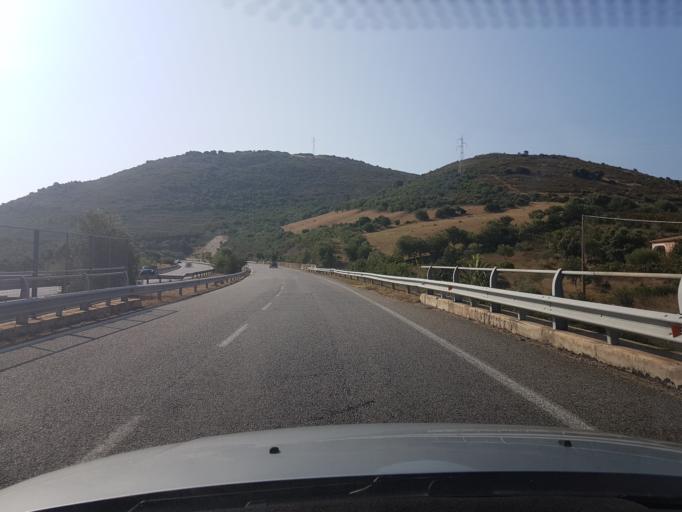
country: IT
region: Sardinia
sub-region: Provincia di Olbia-Tempio
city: San Teodoro
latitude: 40.7292
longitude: 9.6510
